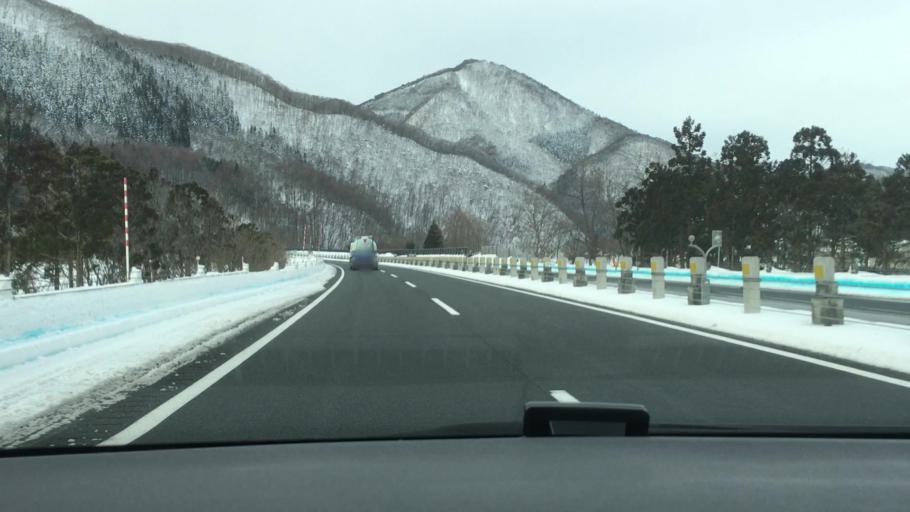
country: JP
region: Akita
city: Hanawa
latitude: 40.1363
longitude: 140.9478
